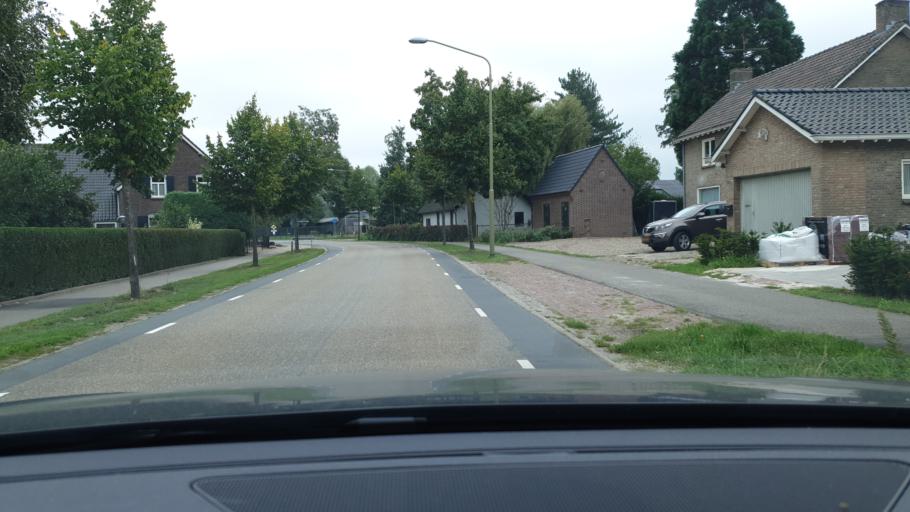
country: NL
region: North Brabant
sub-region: Gemeente Landerd
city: Reek
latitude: 51.7440
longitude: 5.6631
